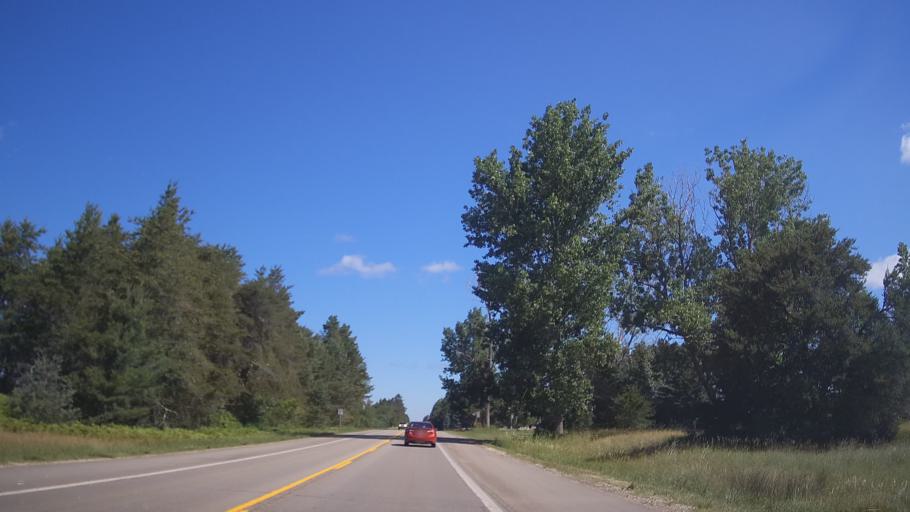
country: US
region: Michigan
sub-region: Cheboygan County
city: Indian River
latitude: 45.4981
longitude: -84.7812
